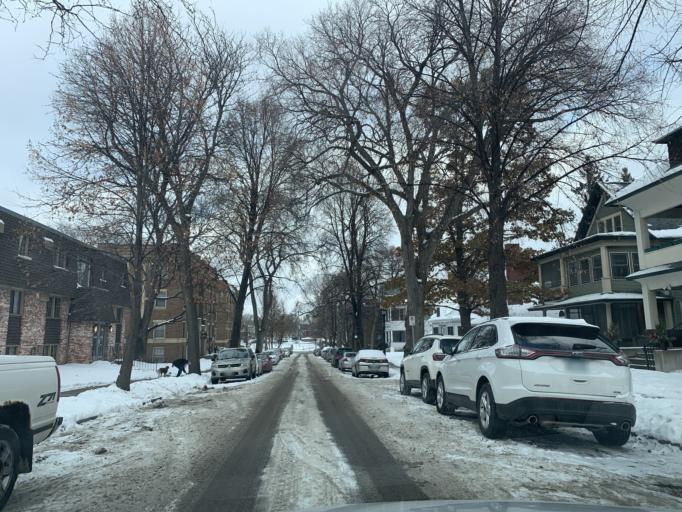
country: US
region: Minnesota
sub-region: Hennepin County
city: Minneapolis
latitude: 44.9541
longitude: -93.2957
